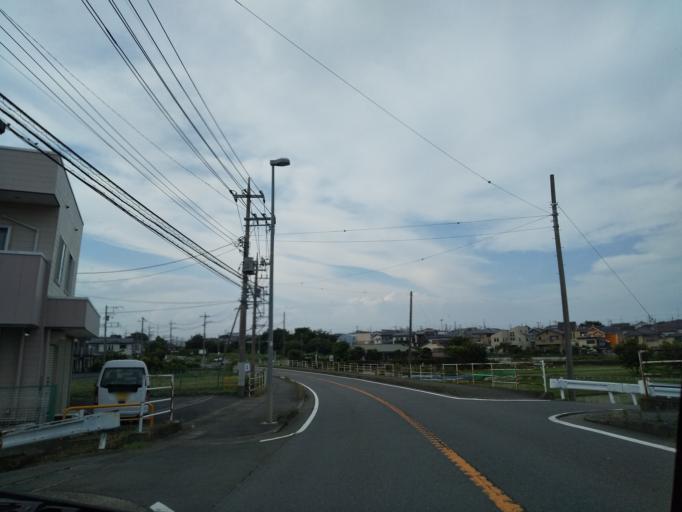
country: JP
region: Kanagawa
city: Atsugi
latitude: 35.4720
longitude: 139.3412
